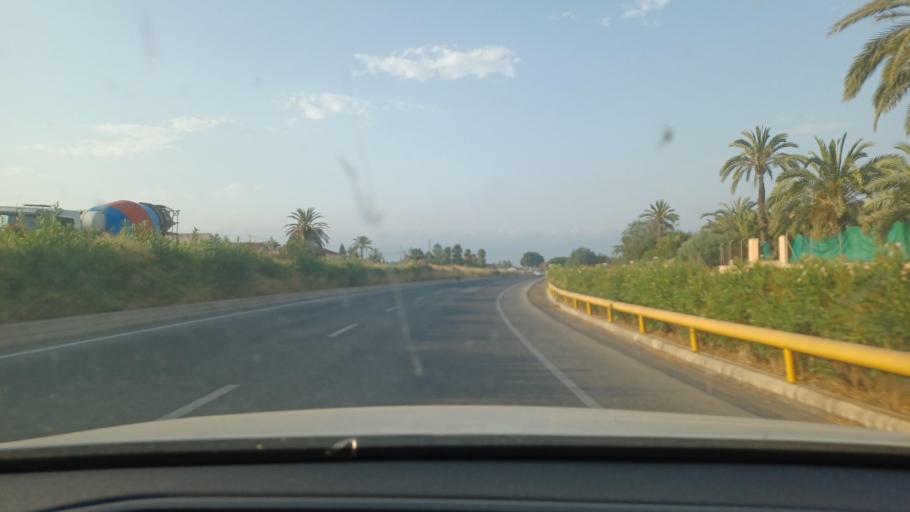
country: ES
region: Valencia
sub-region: Provincia de Alicante
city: Elche
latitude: 38.2194
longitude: -0.6972
